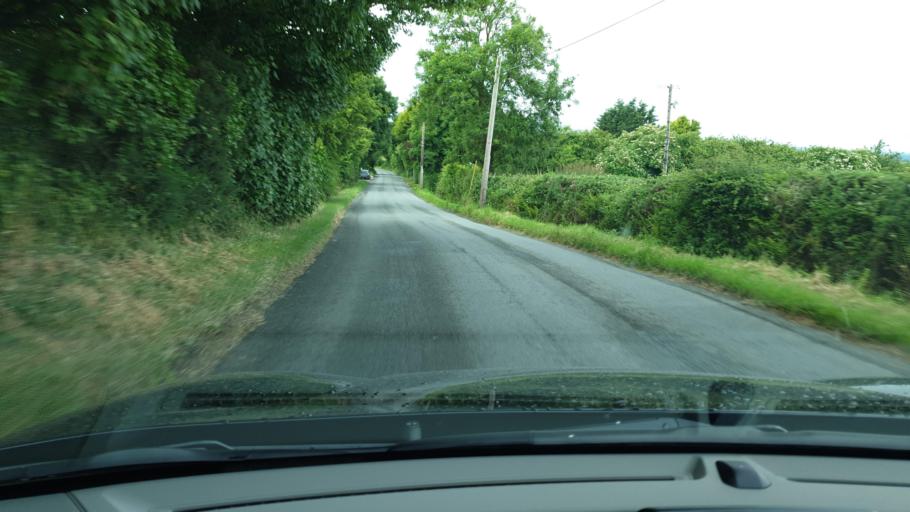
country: IE
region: Leinster
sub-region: An Mhi
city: Ashbourne
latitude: 53.5580
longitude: -6.3957
